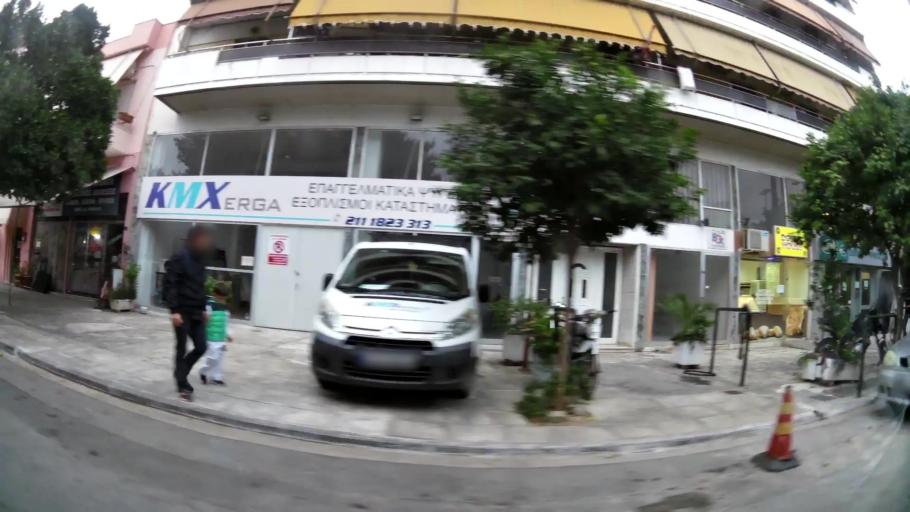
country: GR
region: Attica
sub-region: Nomos Piraios
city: Agios Ioannis Rentis
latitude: 37.9616
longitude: 23.6753
